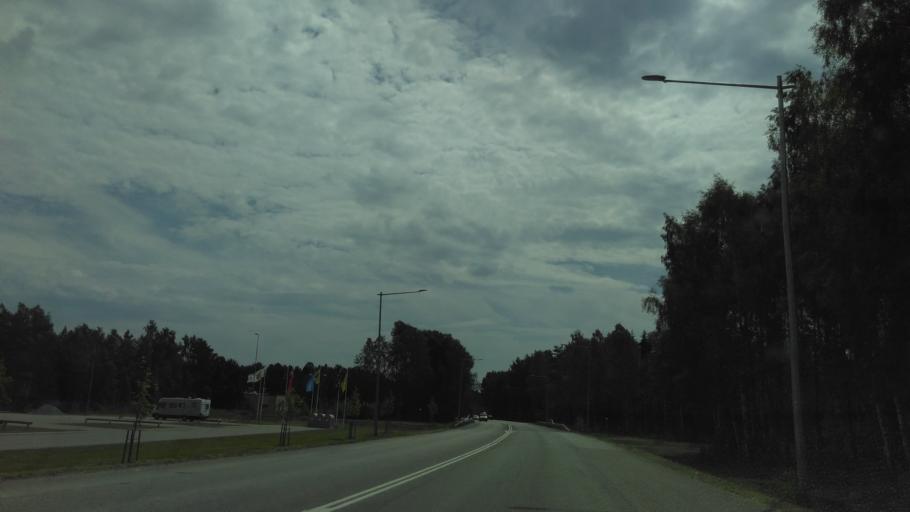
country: SE
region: Vaestra Goetaland
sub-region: Lidkopings Kommun
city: Lidkoping
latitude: 58.4931
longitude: 13.1820
